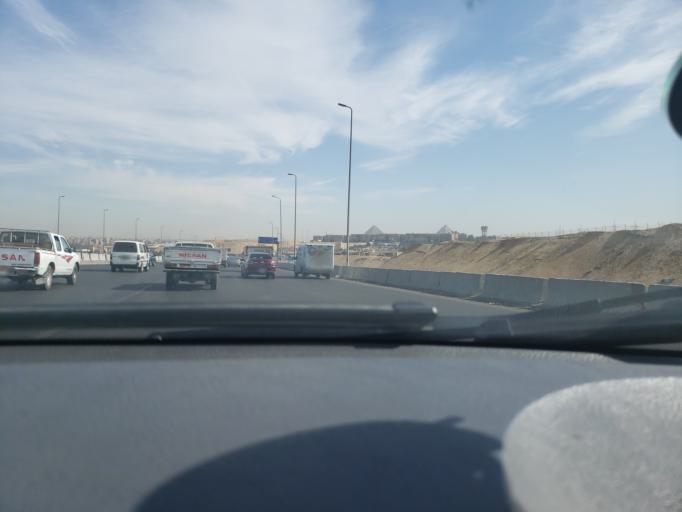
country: EG
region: Al Jizah
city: Al Jizah
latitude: 29.9981
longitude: 31.1019
